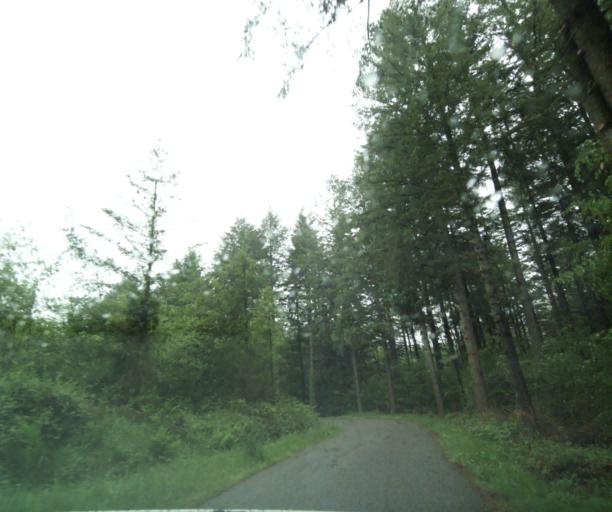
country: FR
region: Bourgogne
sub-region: Departement de Saone-et-Loire
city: Charolles
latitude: 46.3743
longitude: 4.3634
